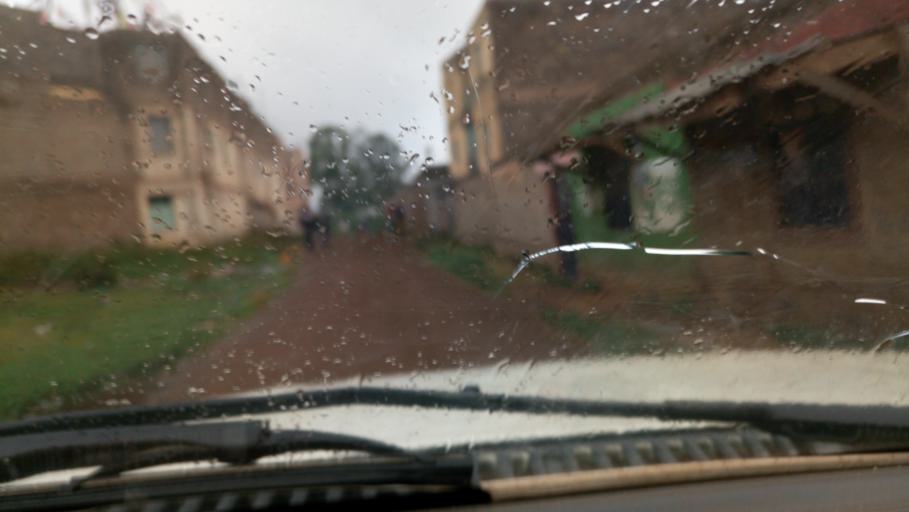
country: KE
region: Kiambu
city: Kiambu
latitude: -1.1902
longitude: 36.9108
